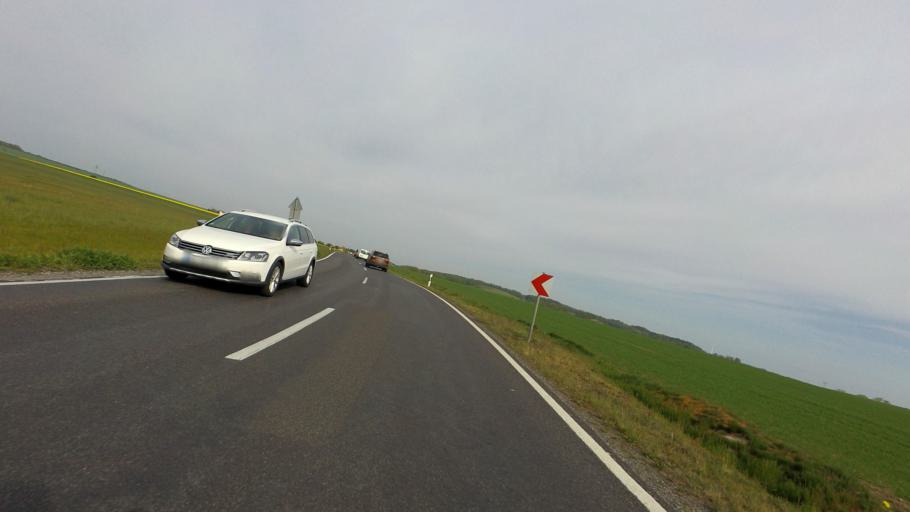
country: DE
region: Saxony
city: Arnsdorf
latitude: 51.1090
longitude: 13.9712
